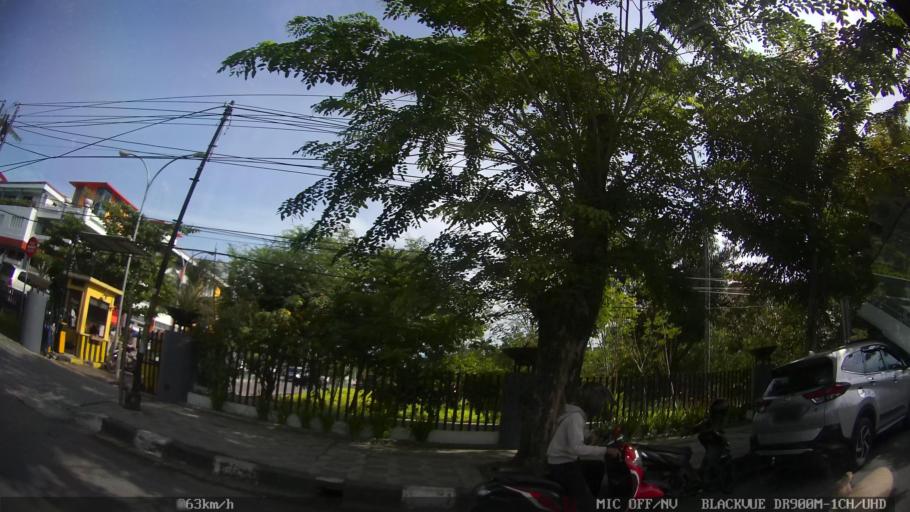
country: ID
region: North Sumatra
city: Medan
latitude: 3.5675
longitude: 98.6580
